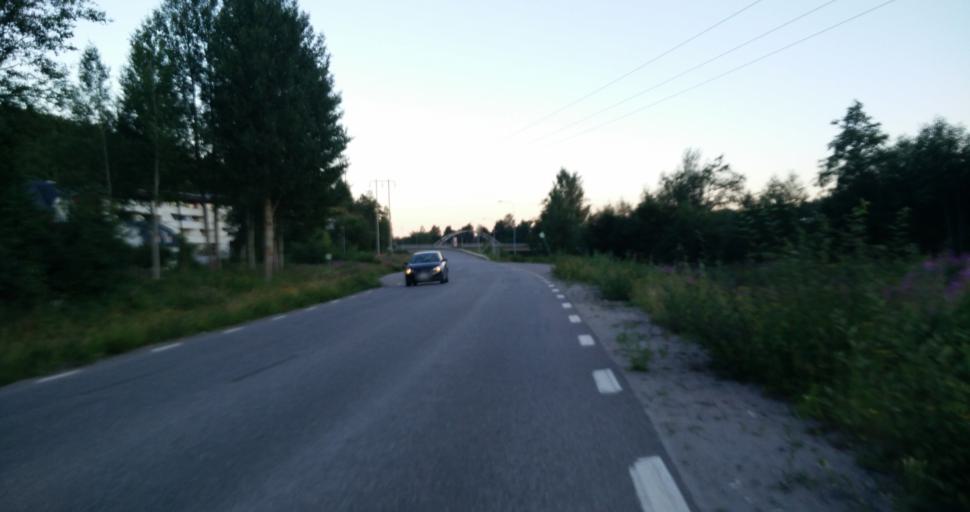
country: SE
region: Vaesternorrland
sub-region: Sundsvalls Kommun
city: Skottsund
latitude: 62.3052
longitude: 17.3843
